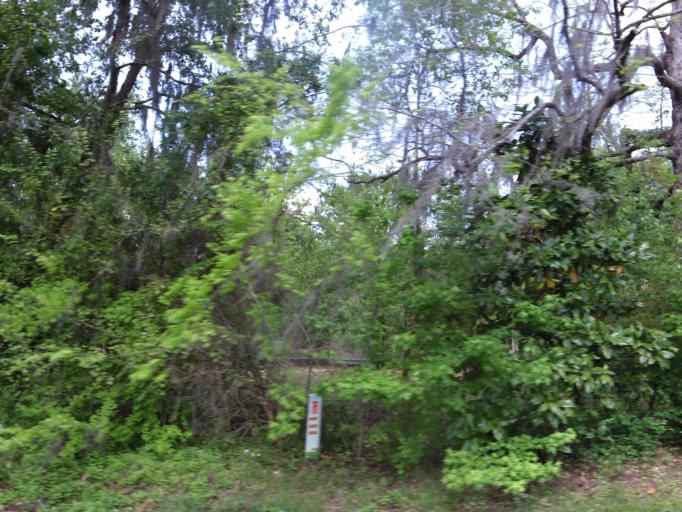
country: US
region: Georgia
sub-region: Camden County
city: Kingsland
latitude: 30.7861
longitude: -81.7046
